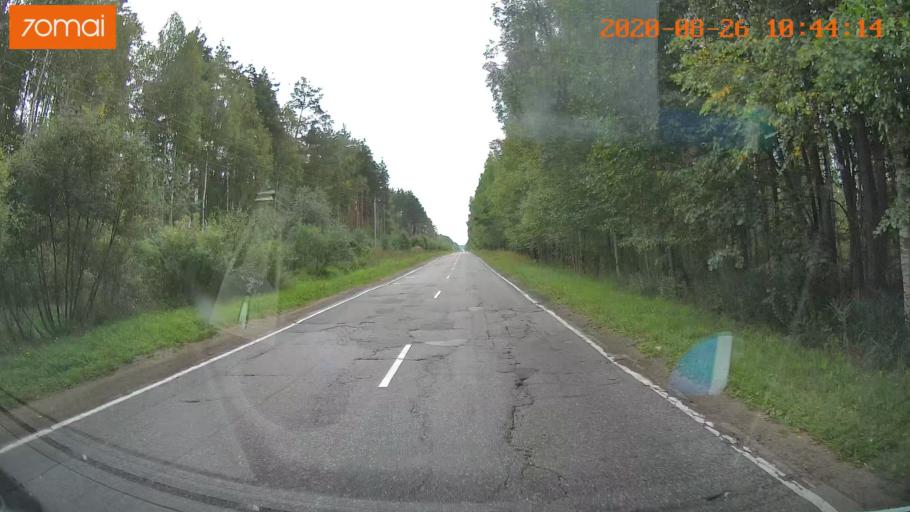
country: RU
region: Rjazan
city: Lashma
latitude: 54.7727
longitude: 41.1829
